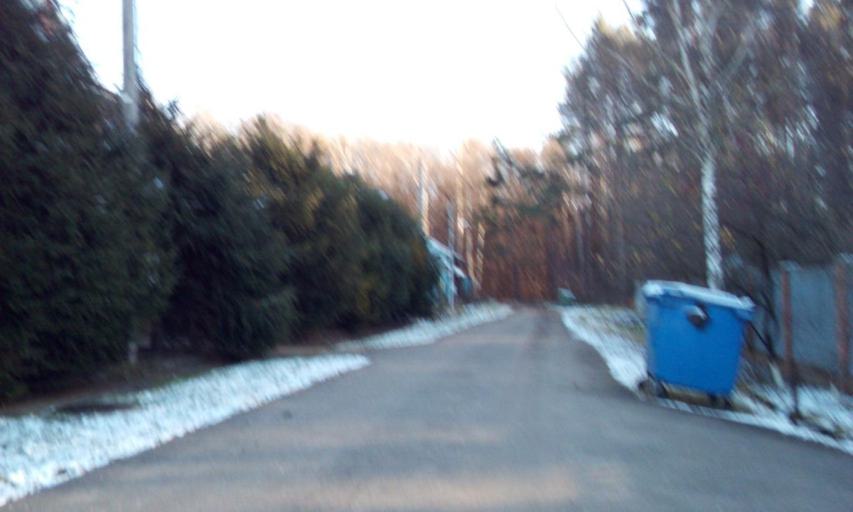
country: RU
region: Moskovskaya
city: Aprelevka
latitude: 55.5550
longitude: 37.0929
